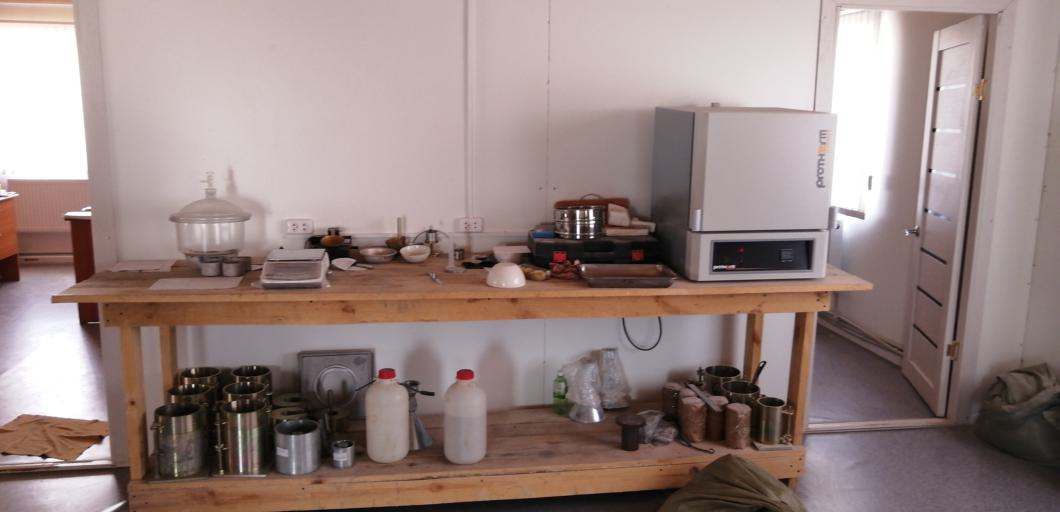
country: KZ
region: Qaraghandy
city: Balqash
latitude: 46.6275
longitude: 74.3775
